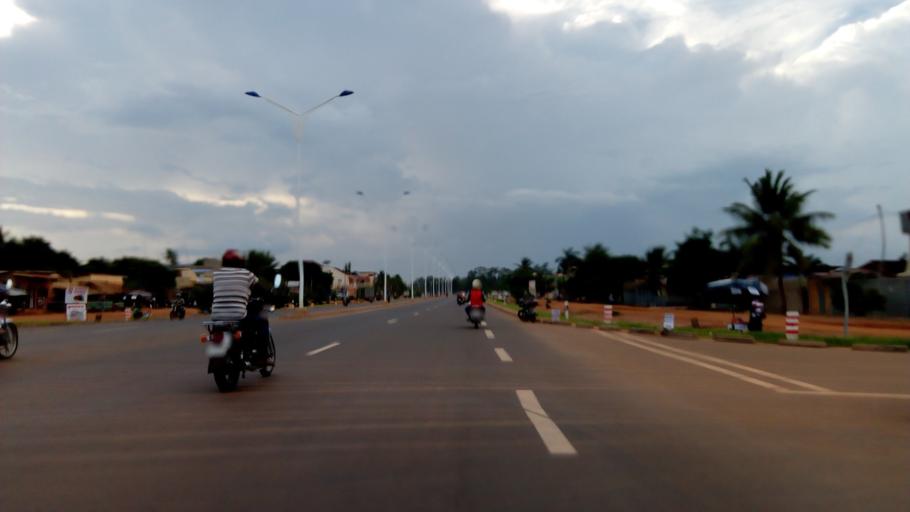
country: TG
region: Maritime
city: Lome
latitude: 6.2433
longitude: 1.1958
